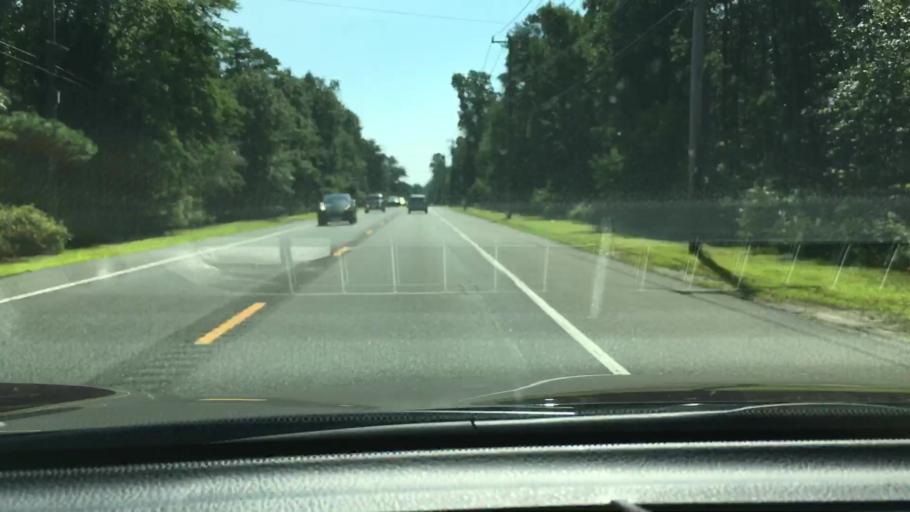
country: US
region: New Jersey
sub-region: Cumberland County
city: Laurel Lake
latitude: 39.3759
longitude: -74.9530
